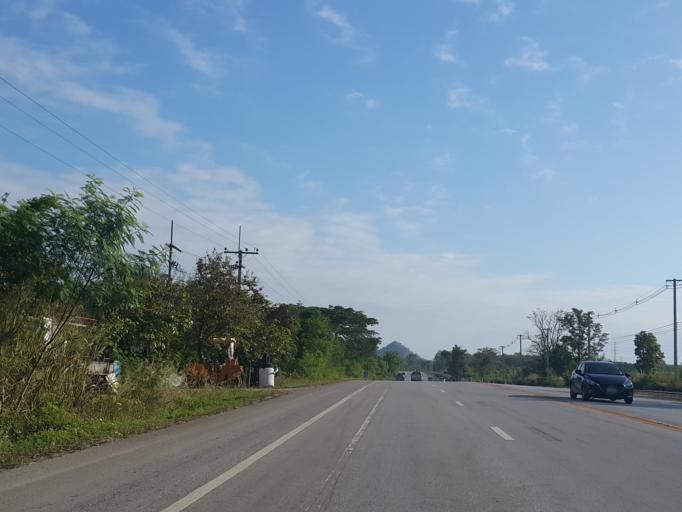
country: TH
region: Lampang
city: Mae Mo
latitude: 18.2526
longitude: 99.6069
